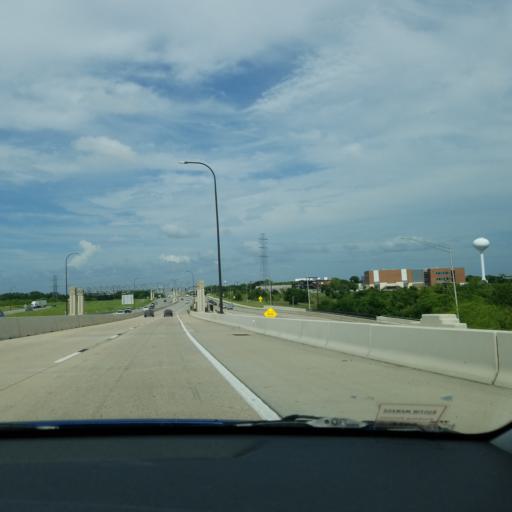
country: US
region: Texas
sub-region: Travis County
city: Manor
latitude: 30.3443
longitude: -97.5798
